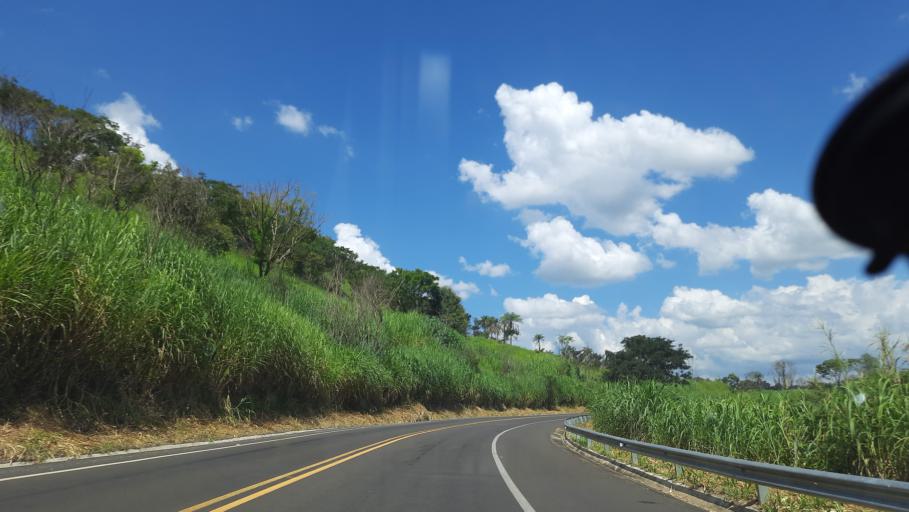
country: BR
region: Sao Paulo
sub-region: Sao Jose Do Rio Pardo
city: Sao Jose do Rio Pardo
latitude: -21.6047
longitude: -46.9688
